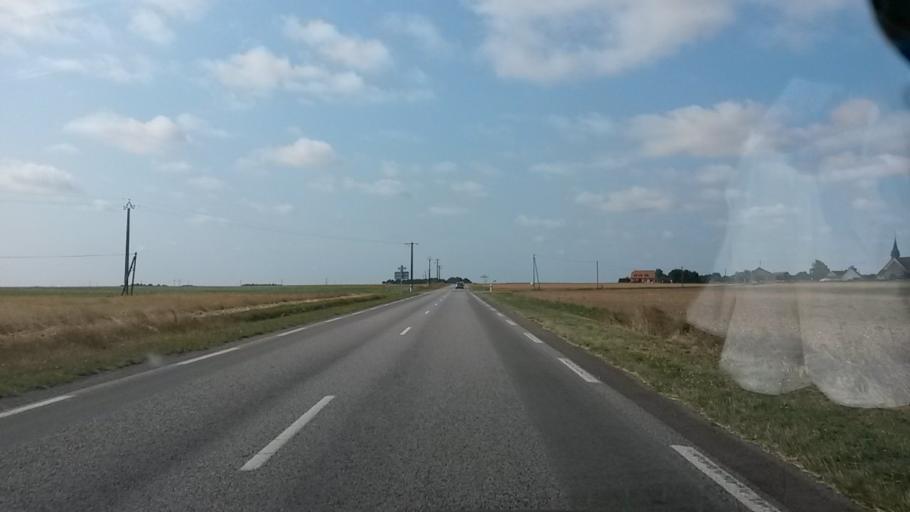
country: FR
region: Haute-Normandie
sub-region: Departement de l'Eure
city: Tillieres-sur-Avre
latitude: 48.8082
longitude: 1.0017
